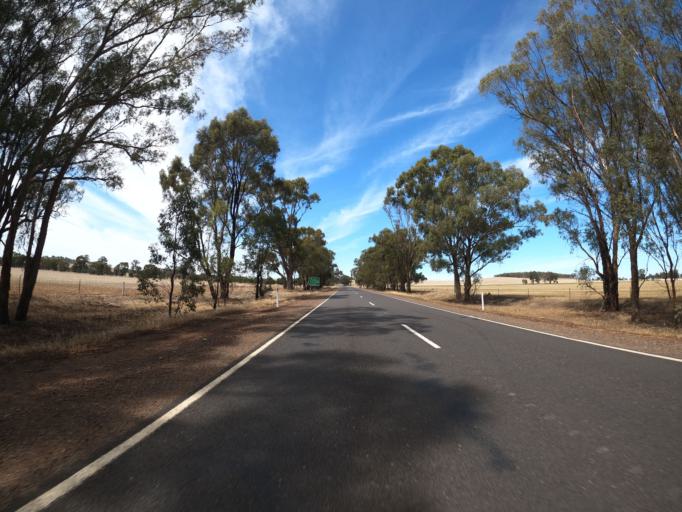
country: AU
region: Victoria
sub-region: Benalla
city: Benalla
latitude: -36.3152
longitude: 145.9583
